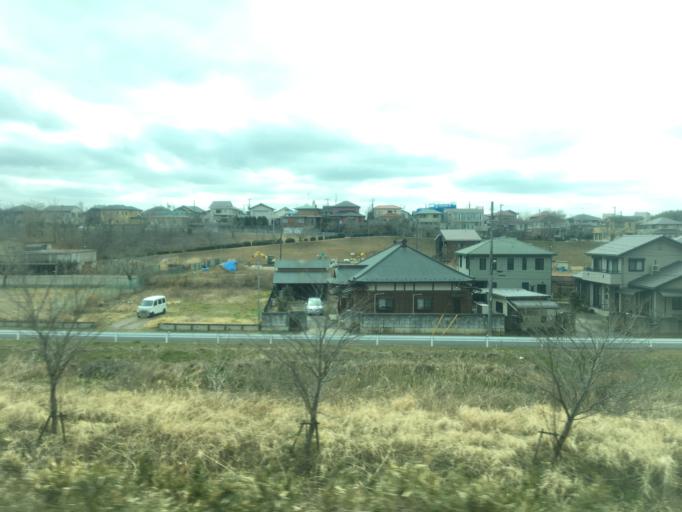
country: JP
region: Chiba
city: Narita
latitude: 35.7864
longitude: 140.3045
